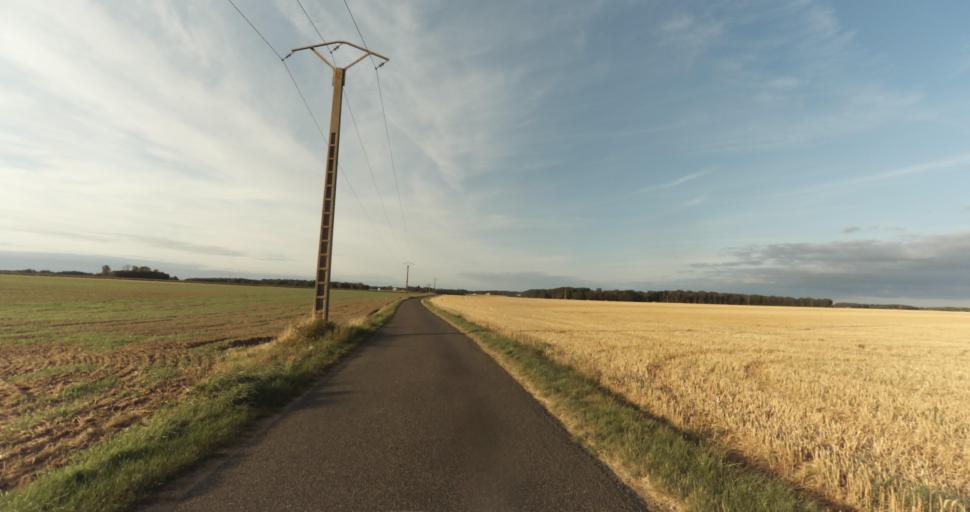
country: FR
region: Haute-Normandie
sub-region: Departement de l'Eure
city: Saint-Germain-sur-Avre
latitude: 48.8237
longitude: 1.2708
